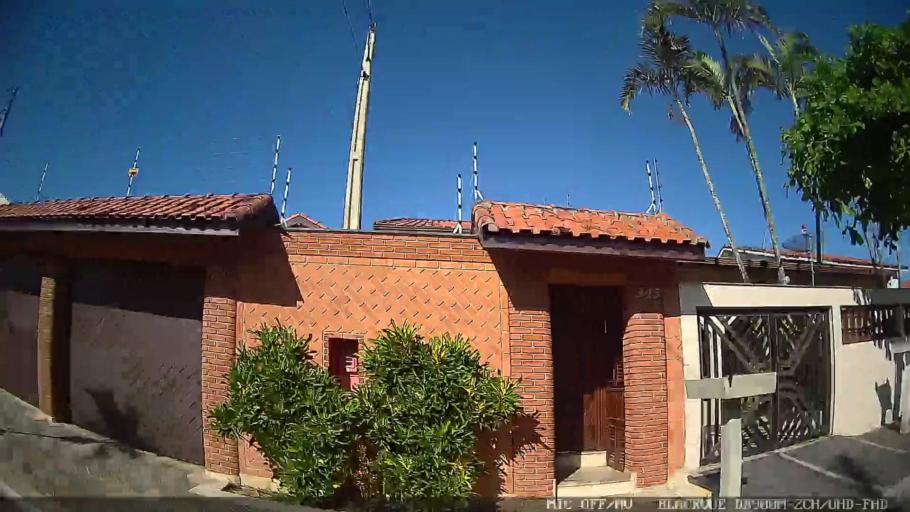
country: BR
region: Sao Paulo
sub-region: Peruibe
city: Peruibe
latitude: -24.2808
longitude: -46.9481
